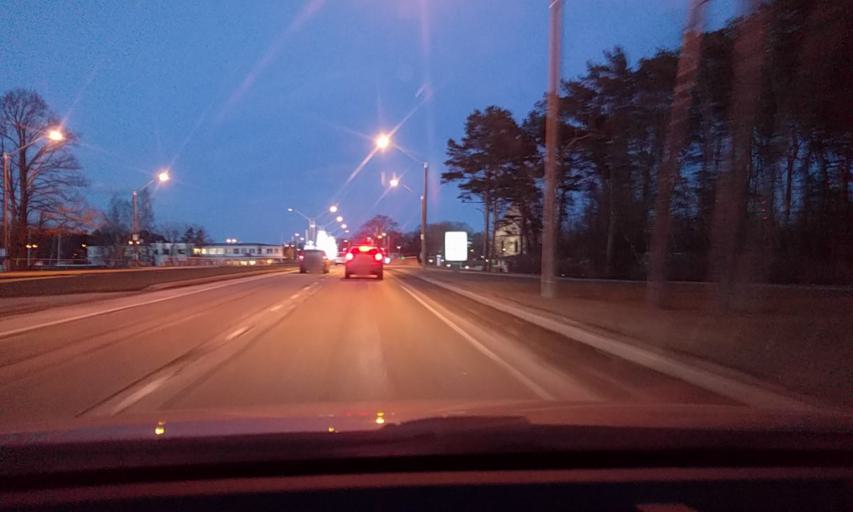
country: EE
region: Harju
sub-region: Viimsi vald
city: Viimsi
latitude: 59.4649
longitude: 24.8303
